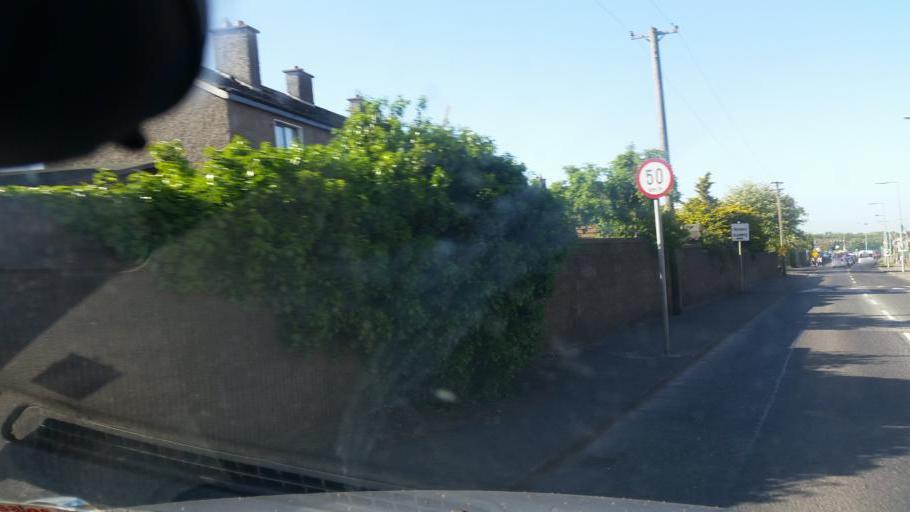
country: IE
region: Leinster
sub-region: Fingal County
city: Blanchardstown
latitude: 53.4074
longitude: -6.3925
